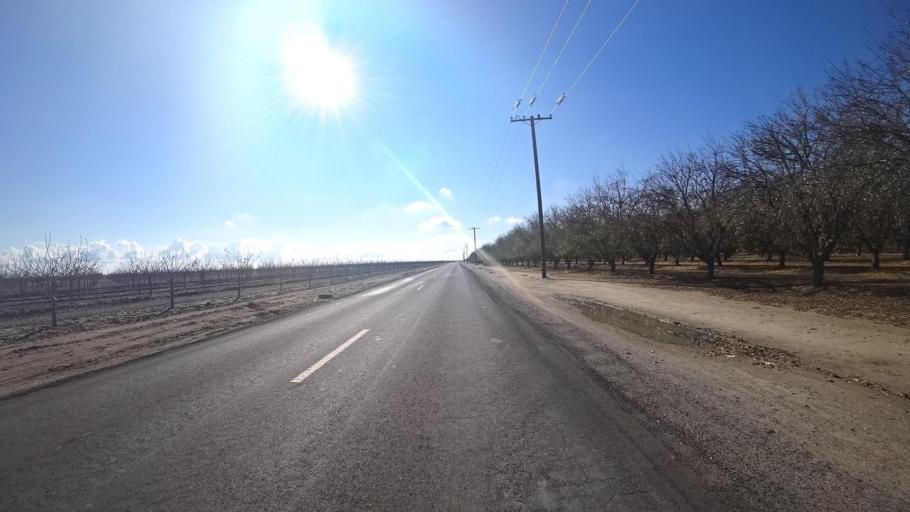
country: US
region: California
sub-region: Kern County
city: Delano
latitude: 35.7351
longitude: -119.2584
